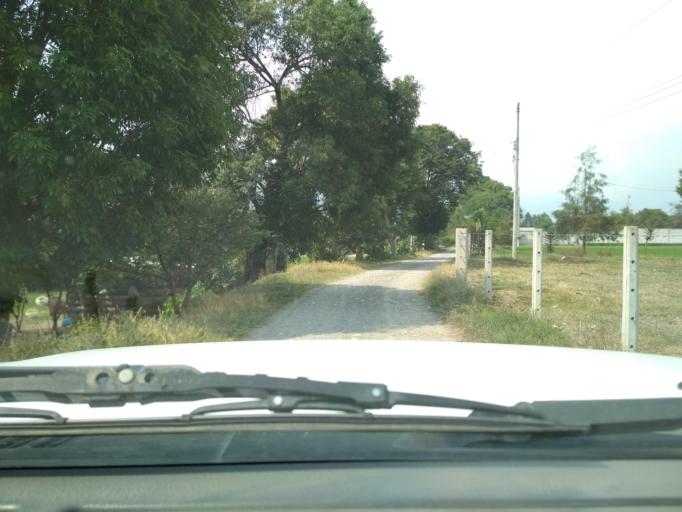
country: MX
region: Veracruz
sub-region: Acultzingo
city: Acatla
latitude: 18.7549
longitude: -97.2274
